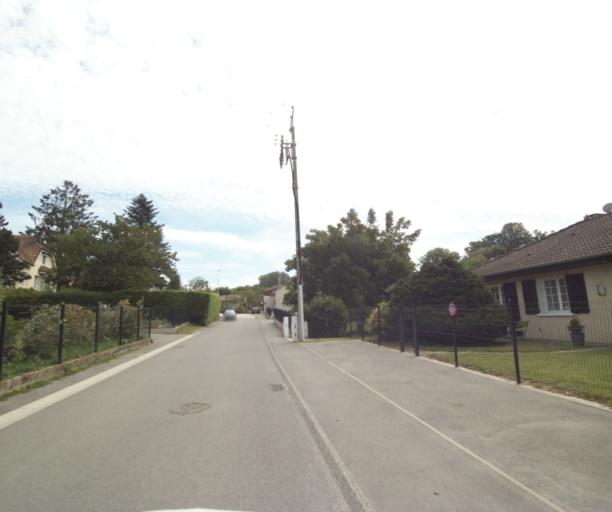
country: FR
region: Rhone-Alpes
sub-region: Departement de la Haute-Savoie
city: Margencel
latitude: 46.3381
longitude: 6.4199
